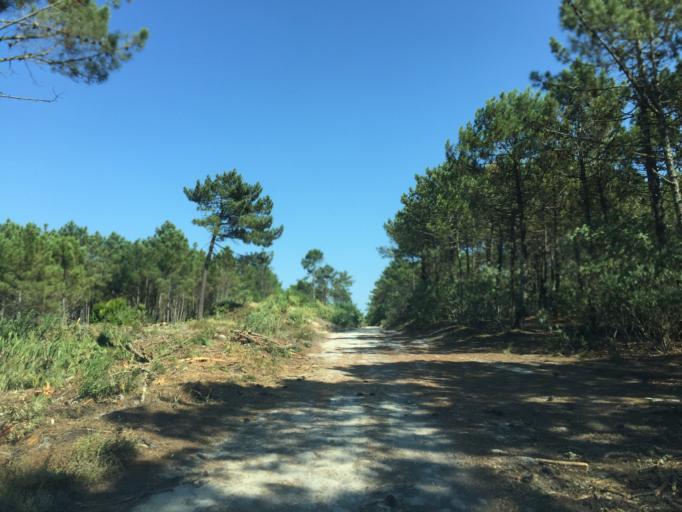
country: PT
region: Coimbra
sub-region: Figueira da Foz
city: Tavarede
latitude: 40.2612
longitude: -8.8539
